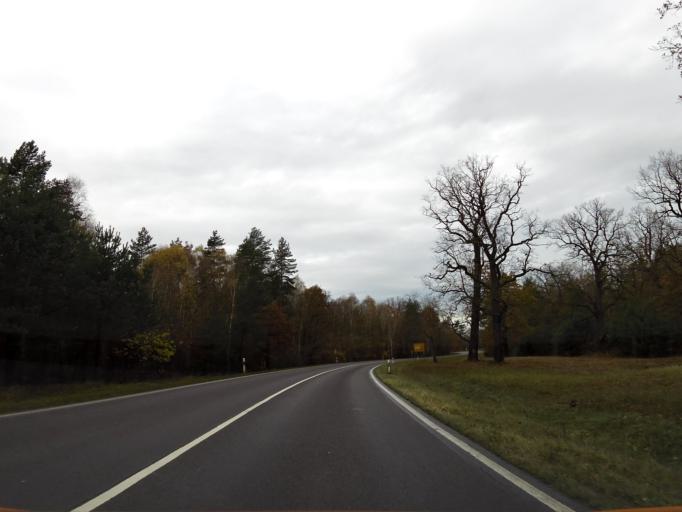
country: DE
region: Saxony-Anhalt
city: Letzlingen
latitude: 52.3468
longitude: 11.4957
